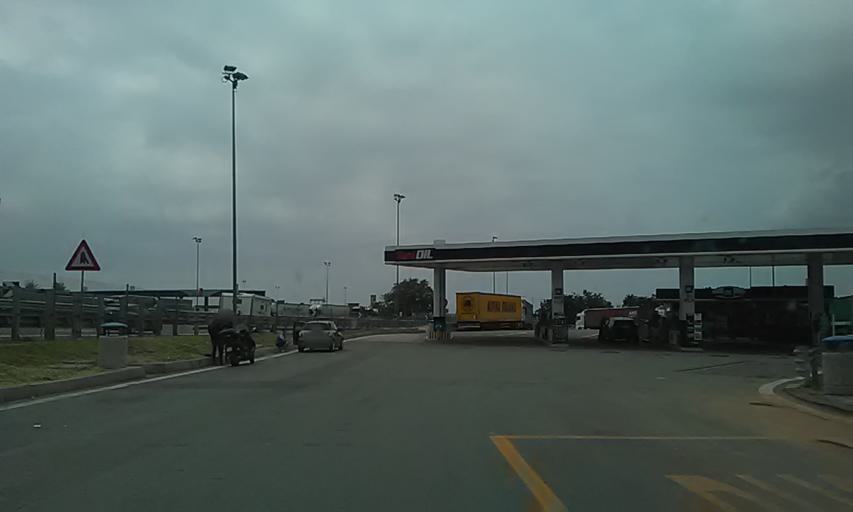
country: IT
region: Liguria
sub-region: Provincia di Genova
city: Mele
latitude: 44.4555
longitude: 8.7444
